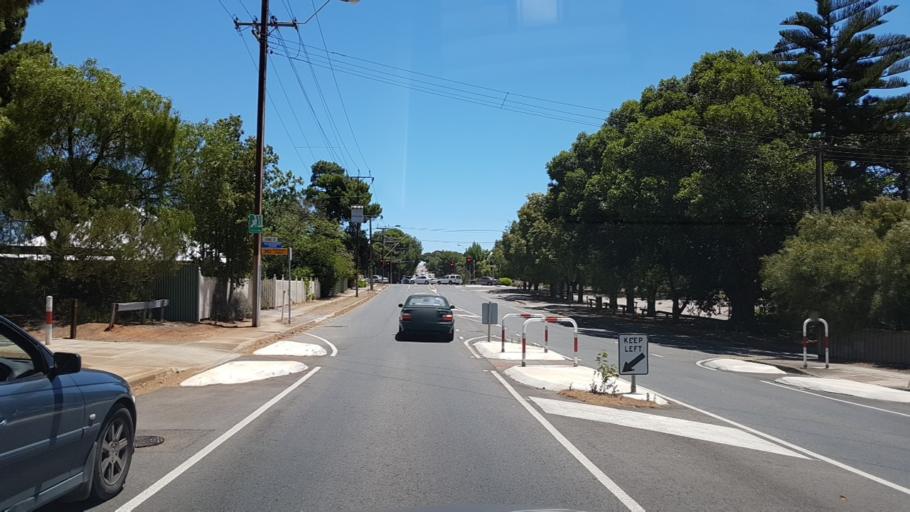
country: AU
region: South Australia
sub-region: Onkaparinga
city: Reynella
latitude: -35.0939
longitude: 138.5406
